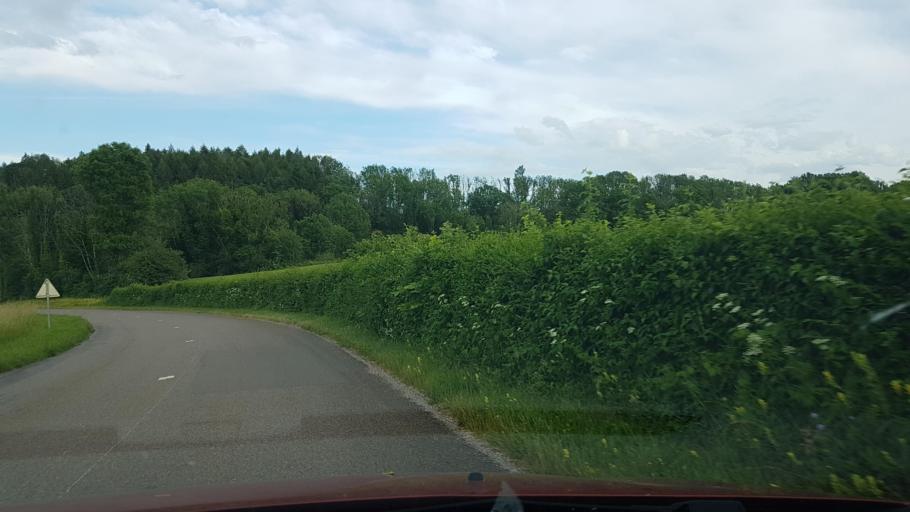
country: FR
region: Franche-Comte
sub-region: Departement du Jura
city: Clairvaux-les-Lacs
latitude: 46.5745
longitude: 5.7408
